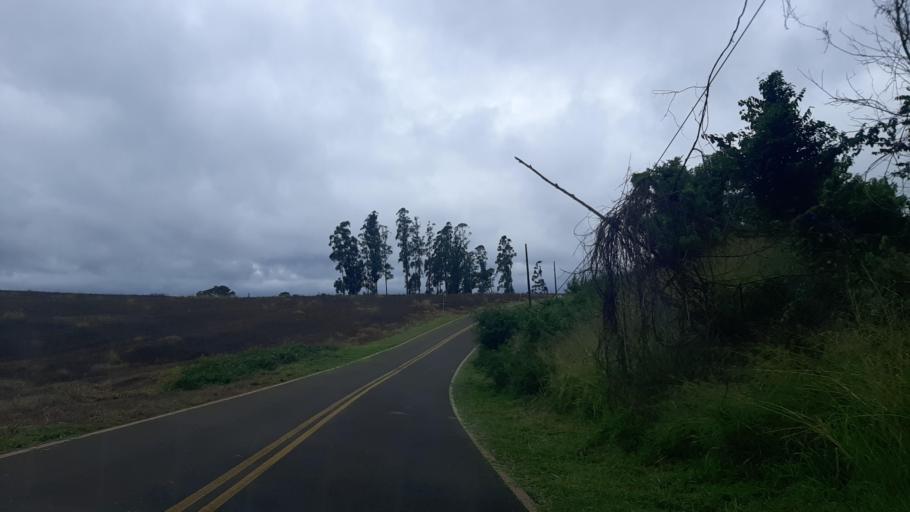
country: BR
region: Parana
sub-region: Ampere
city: Ampere
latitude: -25.9553
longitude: -53.4505
